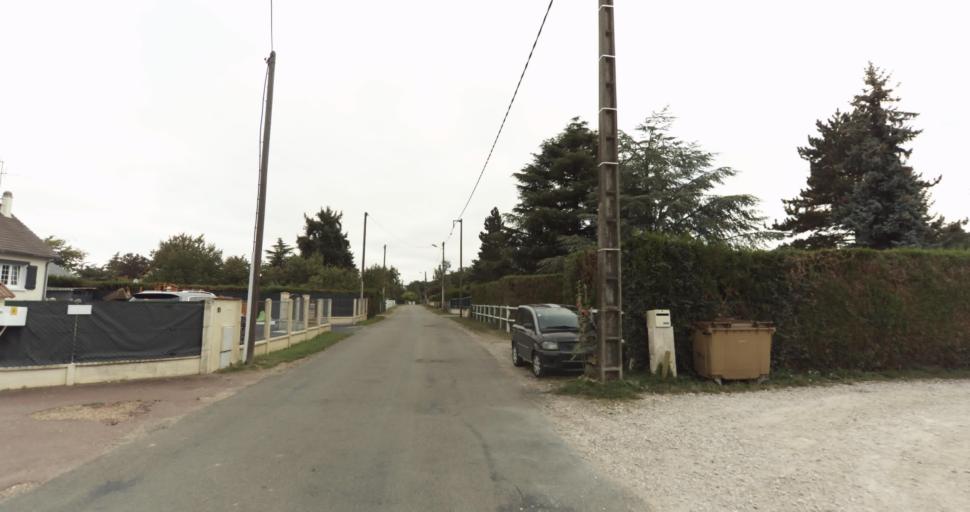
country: FR
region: Haute-Normandie
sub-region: Departement de l'Eure
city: Saint-Germain-sur-Avre
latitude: 48.7700
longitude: 1.2632
